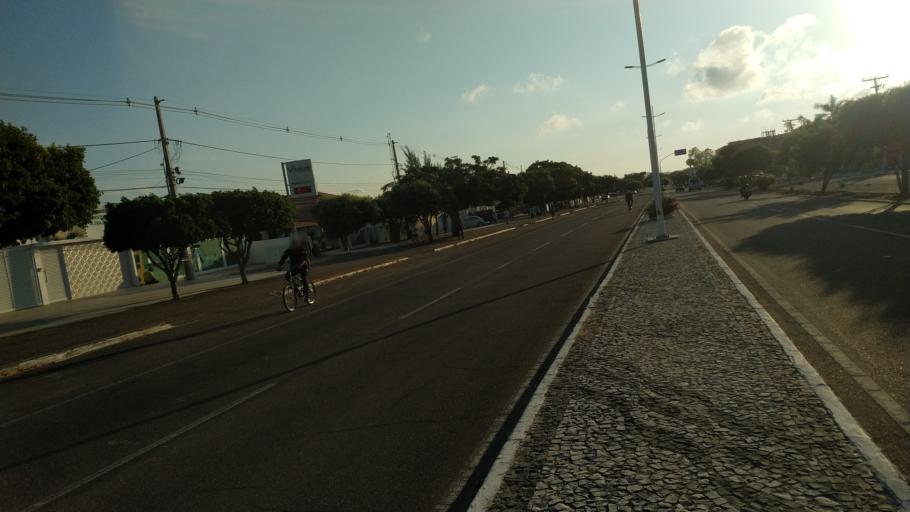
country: BR
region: Bahia
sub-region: Paulo Afonso
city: Paulo Afonso
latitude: -9.3984
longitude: -38.2263
